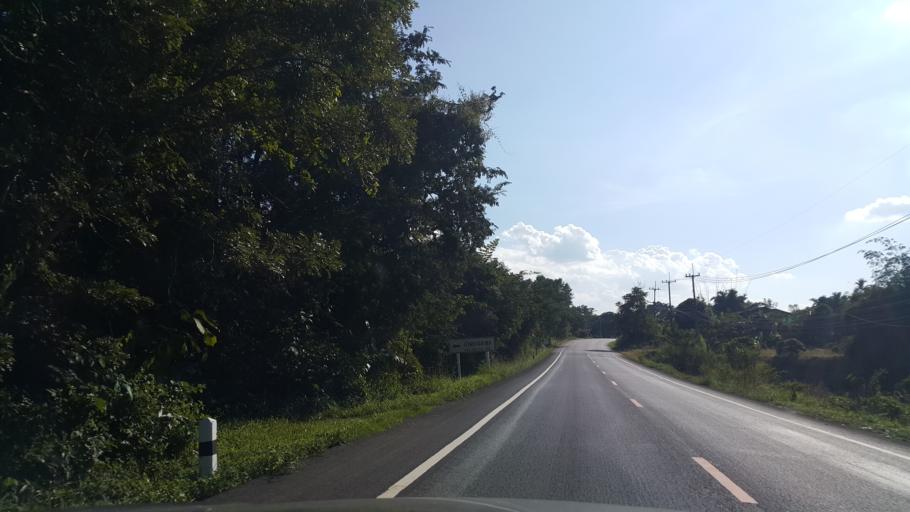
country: TH
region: Lamphun
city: Mae Tha
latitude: 18.4963
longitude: 99.1942
